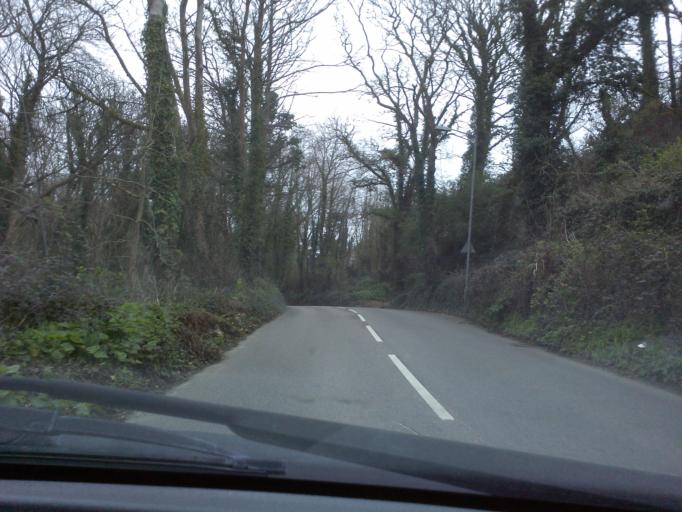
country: GB
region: England
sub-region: Cornwall
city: Penzance
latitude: 50.1088
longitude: -5.5561
